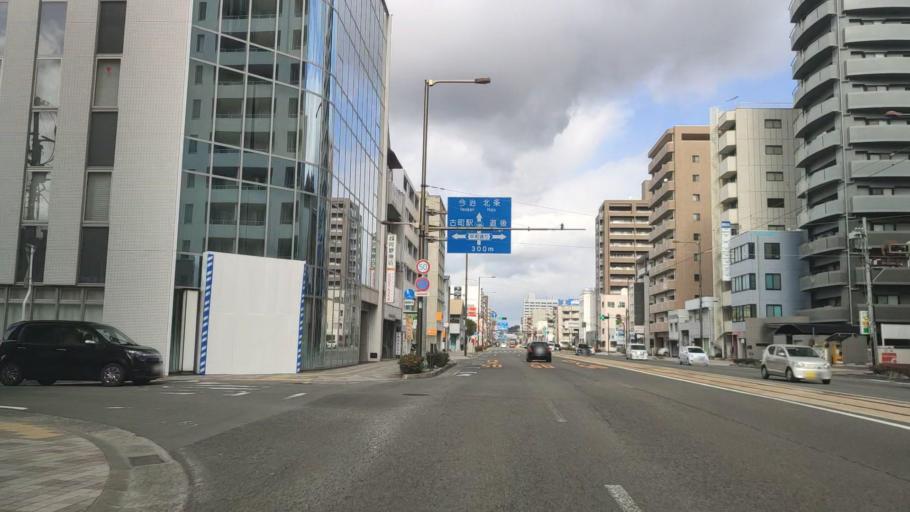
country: JP
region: Ehime
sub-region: Shikoku-chuo Shi
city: Matsuyama
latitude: 33.8454
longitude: 132.7587
